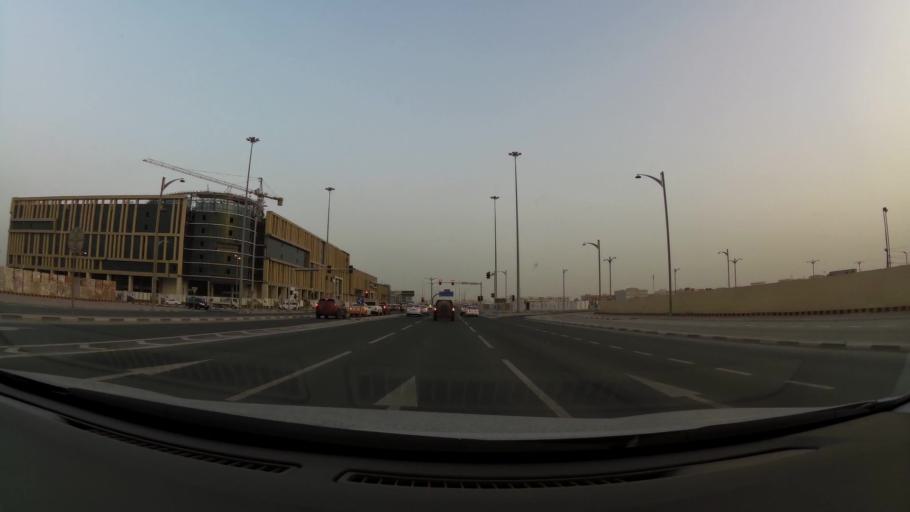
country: QA
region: Baladiyat ad Dawhah
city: Doha
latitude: 25.2538
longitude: 51.4695
